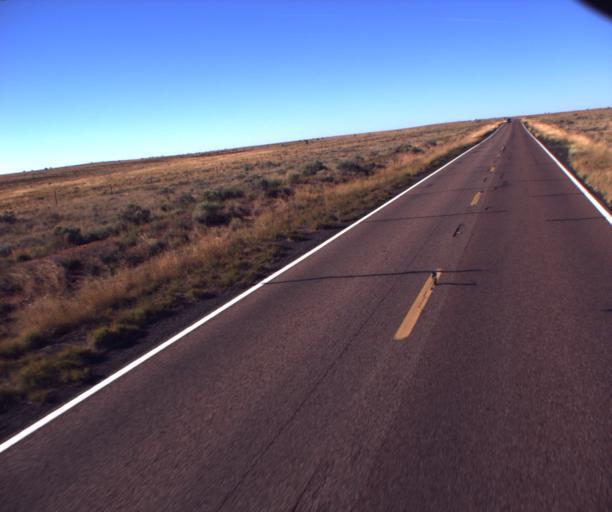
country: US
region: Arizona
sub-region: Navajo County
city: Holbrook
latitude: 34.7800
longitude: -110.2330
